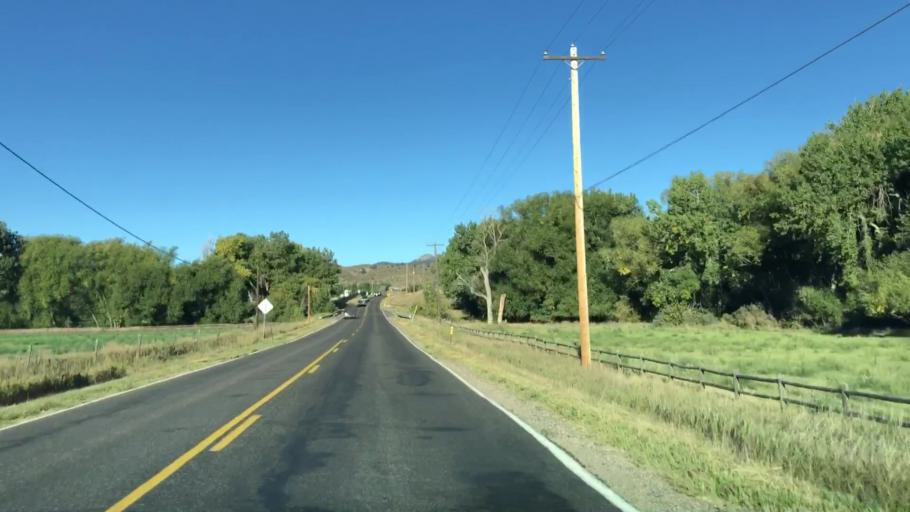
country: US
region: Colorado
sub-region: Larimer County
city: Loveland
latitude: 40.3932
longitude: -105.1640
